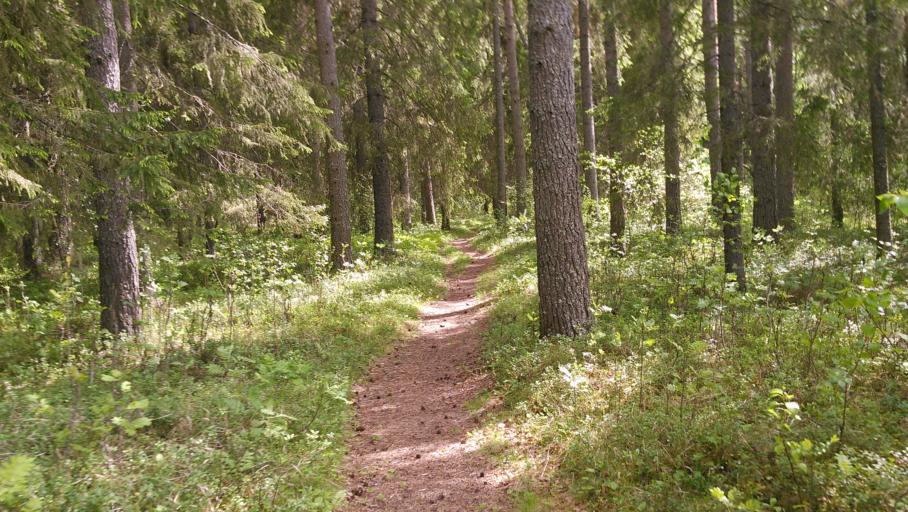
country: SE
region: Vaesterbotten
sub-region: Vannas Kommun
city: Vannasby
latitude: 64.0143
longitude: 19.9035
